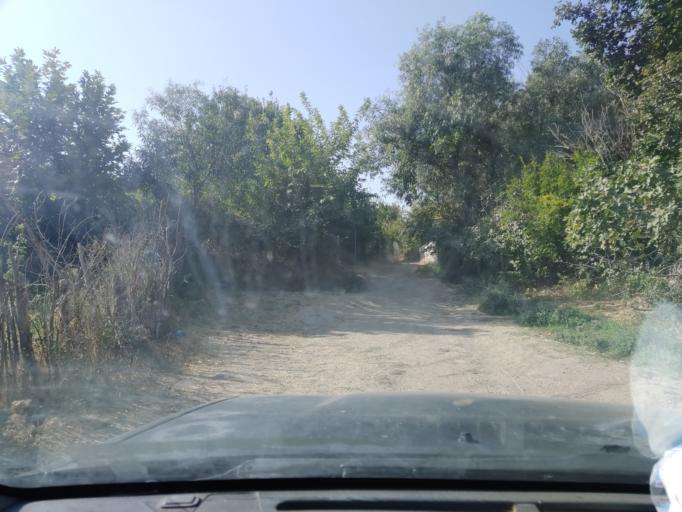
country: IQ
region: As Sulaymaniyah
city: Halabjah
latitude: 35.1636
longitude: 45.9427
